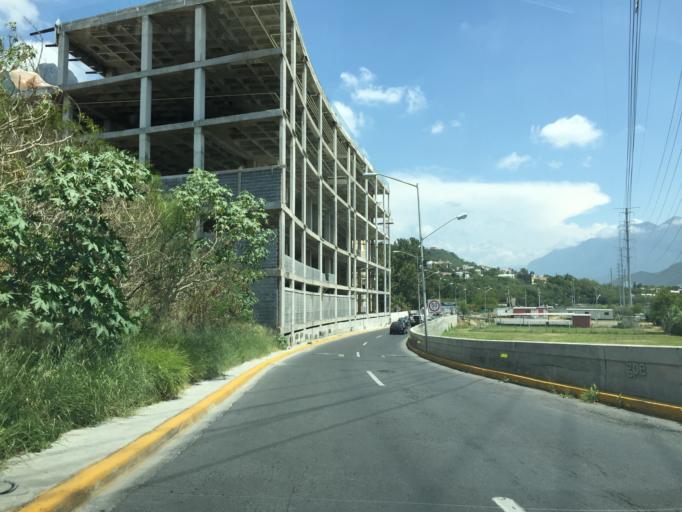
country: MX
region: Nuevo Leon
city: Guadalupe
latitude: 25.6413
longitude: -100.2689
